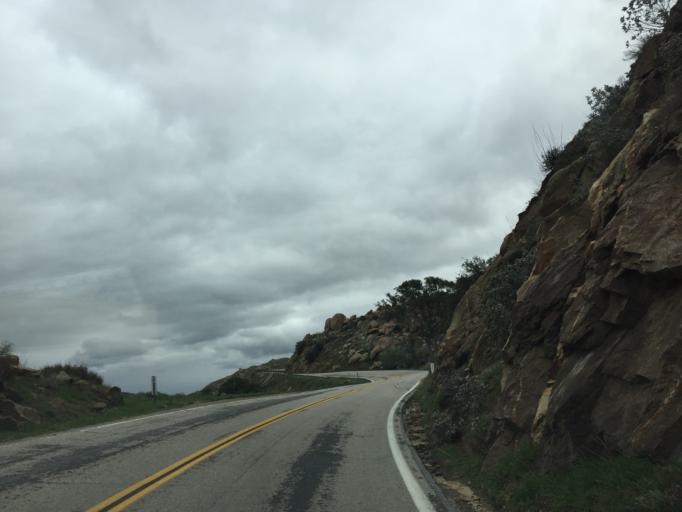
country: US
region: California
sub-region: Riverside County
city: Banning
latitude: 33.9064
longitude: -116.8640
